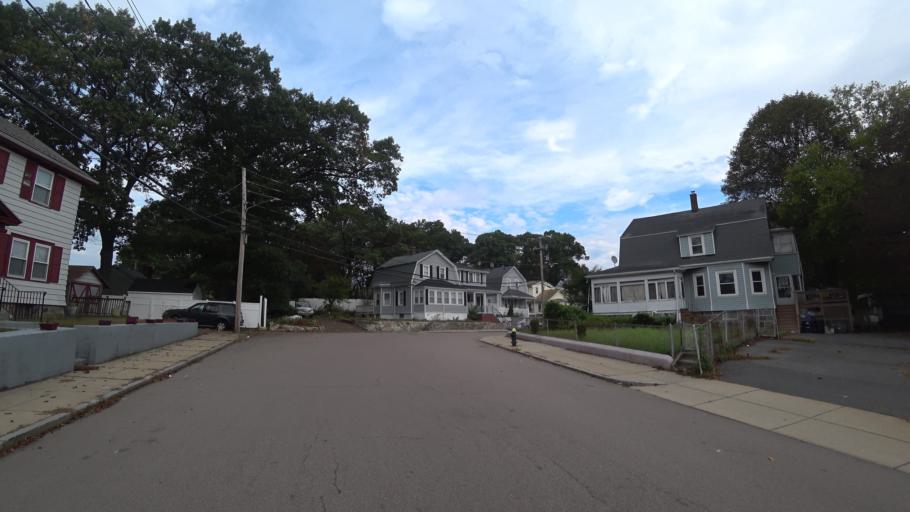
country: US
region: Massachusetts
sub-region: Norfolk County
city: Milton
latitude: 42.2656
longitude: -71.1075
